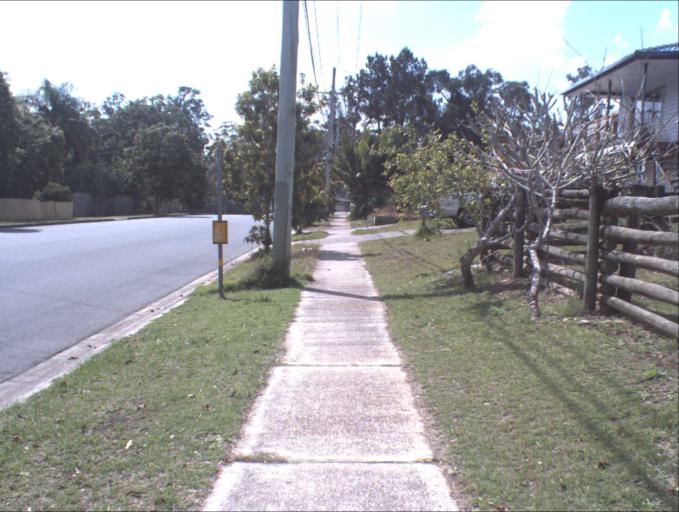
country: AU
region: Queensland
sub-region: Brisbane
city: Sunnybank Hills
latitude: -27.6564
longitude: 153.0455
